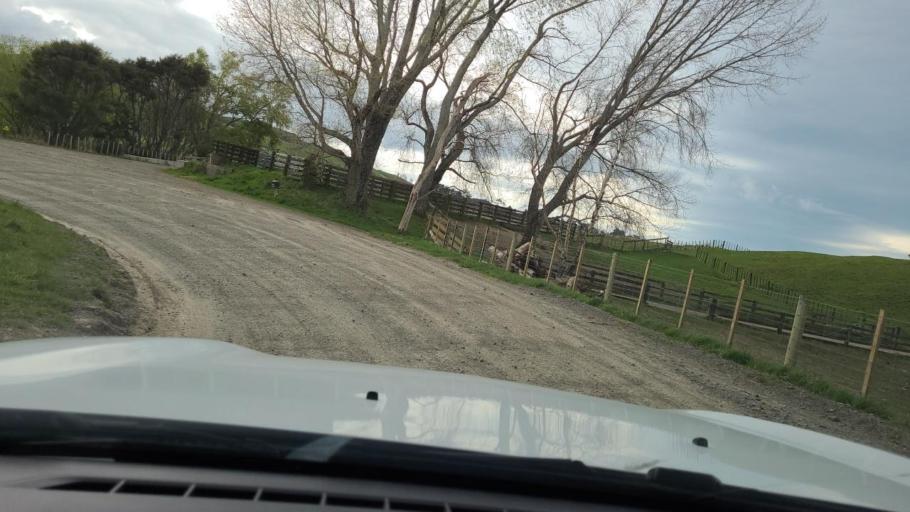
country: NZ
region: Hawke's Bay
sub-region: Napier City
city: Napier
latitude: -39.2966
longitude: 176.8346
